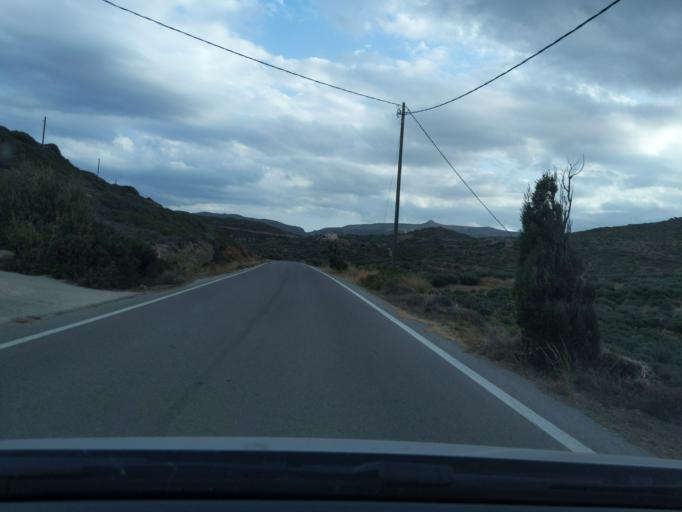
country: GR
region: Crete
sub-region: Nomos Lasithiou
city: Palekastro
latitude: 35.2264
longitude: 26.2562
